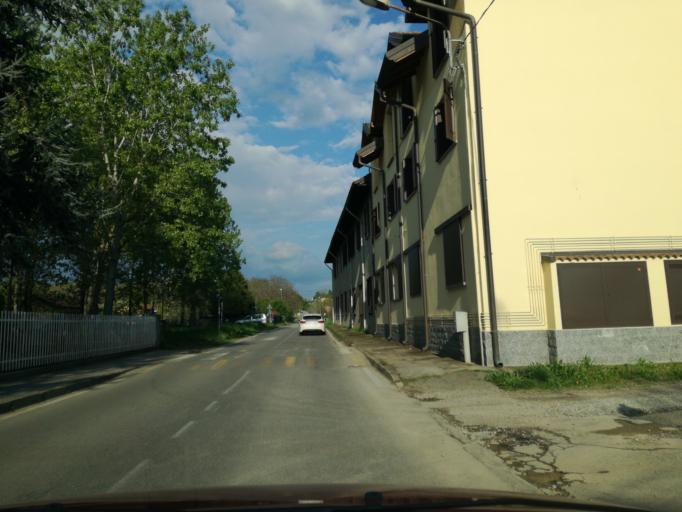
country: IT
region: Lombardy
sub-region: Provincia di Monza e Brianza
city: Usmate-Velate
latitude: 45.6396
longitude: 9.3695
